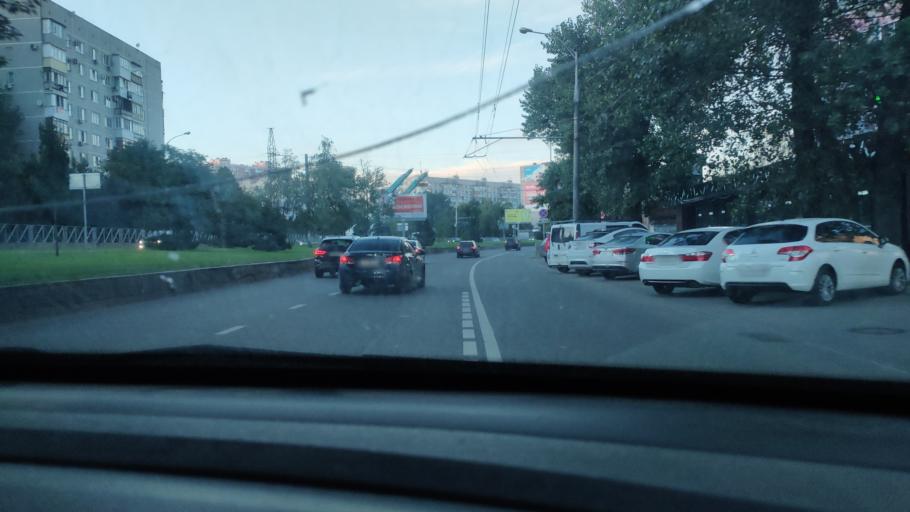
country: RU
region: Krasnodarskiy
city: Krasnodar
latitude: 45.0624
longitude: 38.9611
